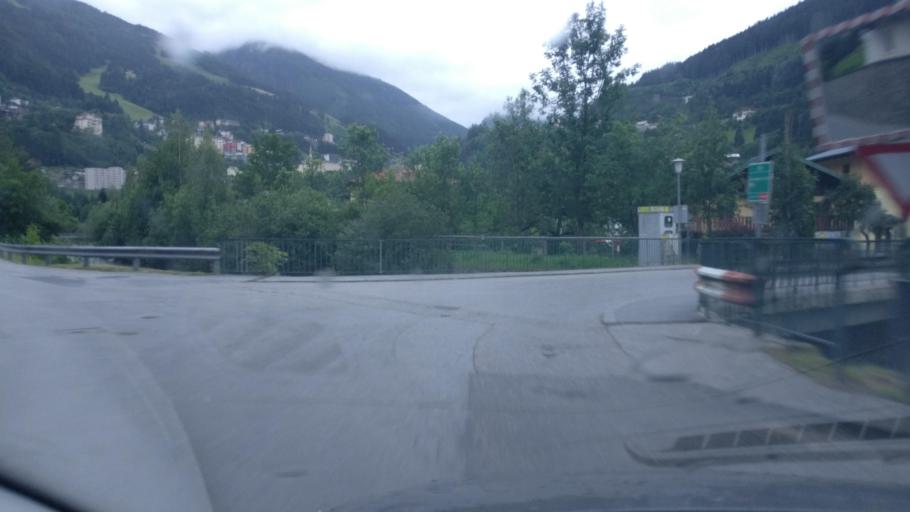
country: AT
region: Salzburg
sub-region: Politischer Bezirk Sankt Johann im Pongau
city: Bad Gastein
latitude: 47.1305
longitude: 13.1363
